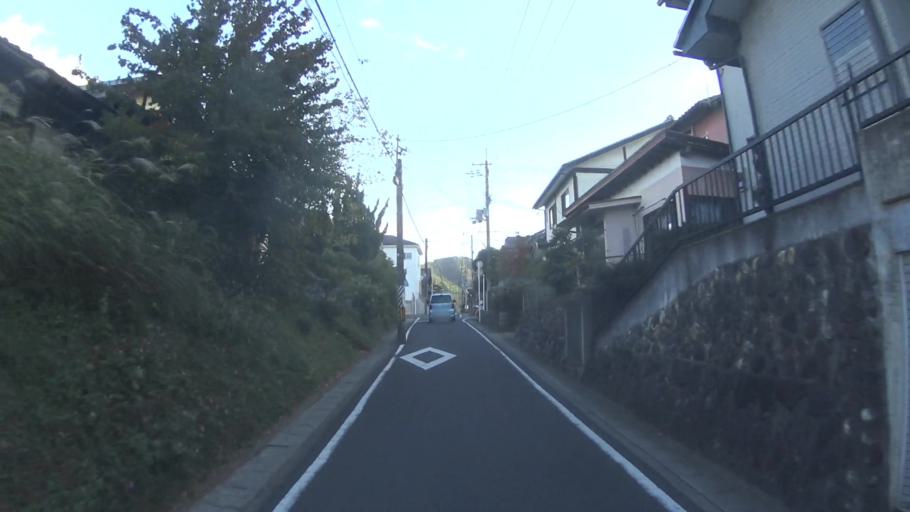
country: JP
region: Kyoto
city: Ayabe
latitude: 35.2956
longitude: 135.2570
